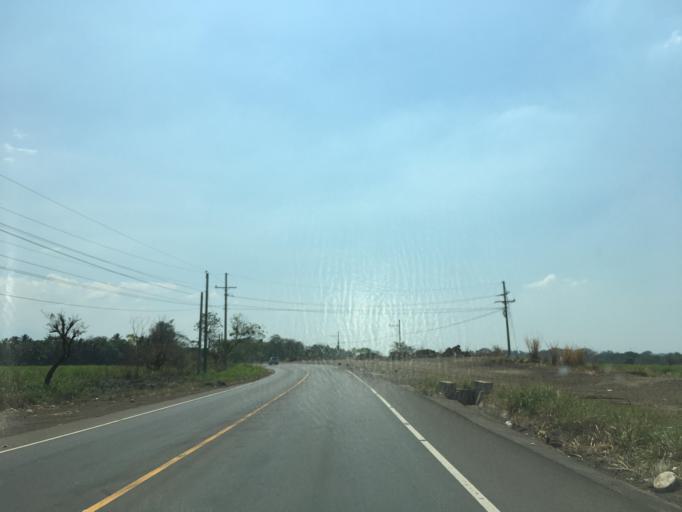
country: GT
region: Escuintla
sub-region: Municipio de Escuintla
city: Escuintla
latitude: 14.2736
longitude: -90.7584
